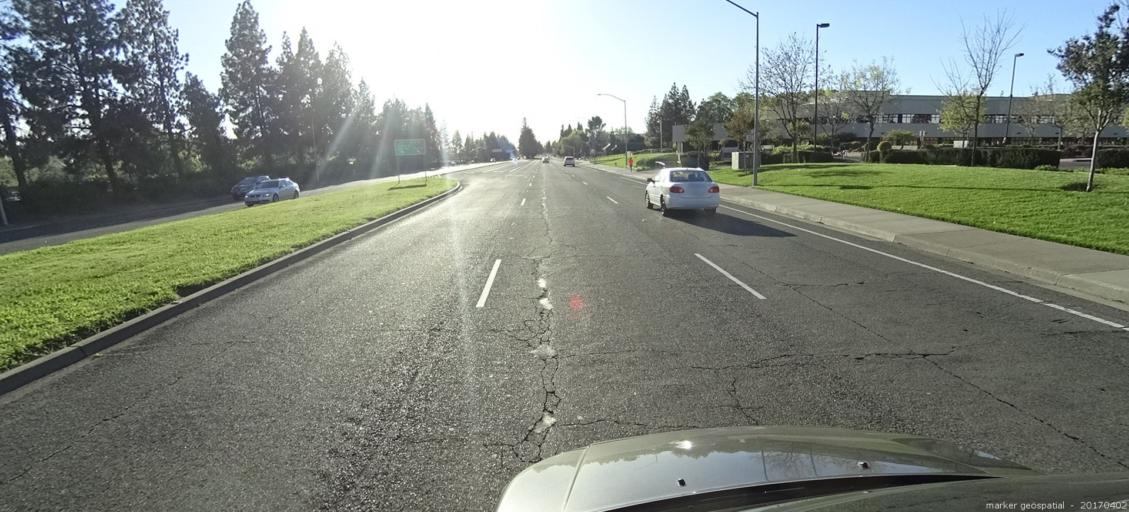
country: US
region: California
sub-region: Sacramento County
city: Arden-Arcade
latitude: 38.5953
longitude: -121.4315
